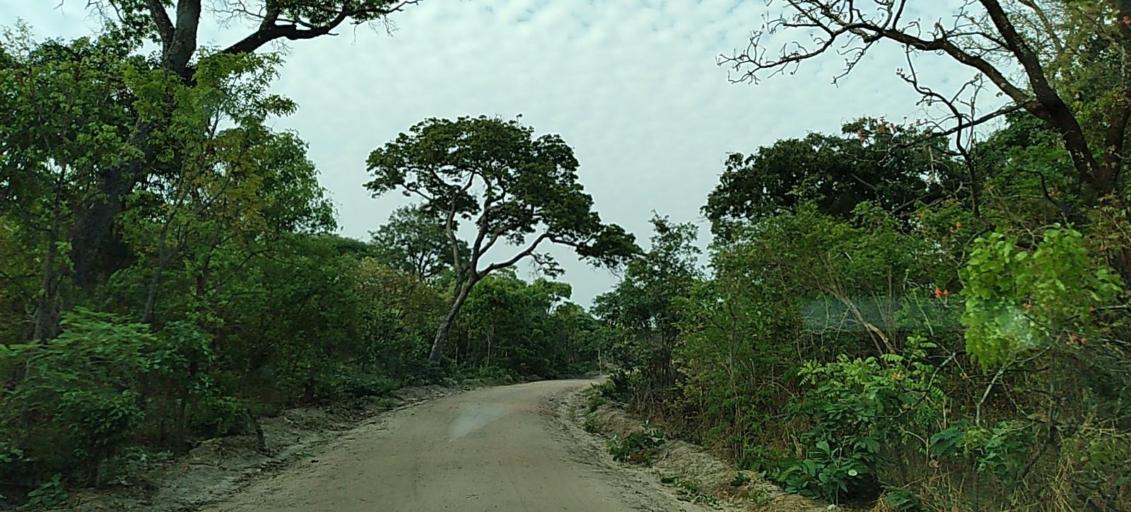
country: ZM
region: Copperbelt
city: Kalulushi
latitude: -12.8948
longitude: 27.6878
